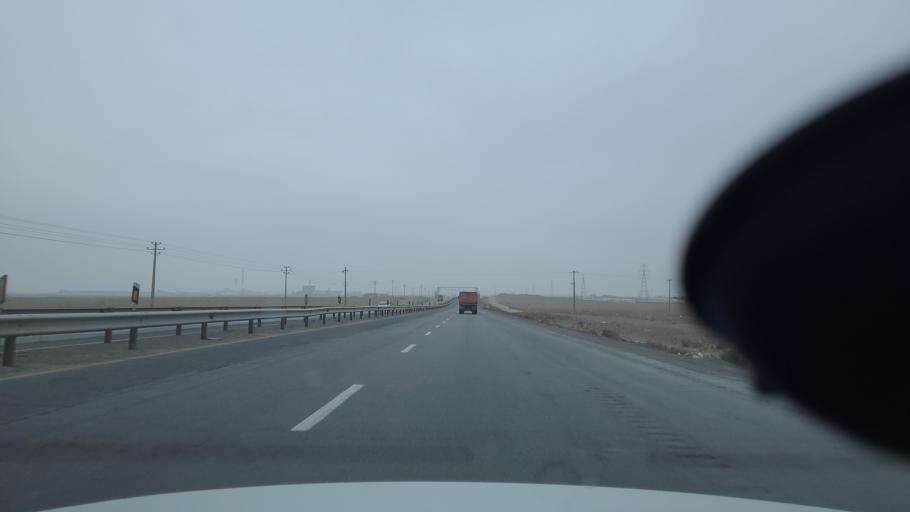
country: IR
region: Razavi Khorasan
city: Fariman
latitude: 35.9561
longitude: 59.7478
